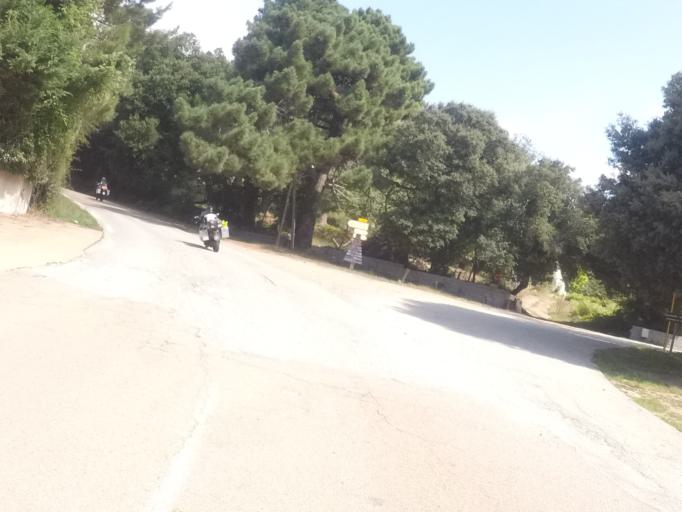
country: FR
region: Corsica
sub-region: Departement de la Corse-du-Sud
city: Zonza
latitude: 41.7600
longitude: 9.1882
